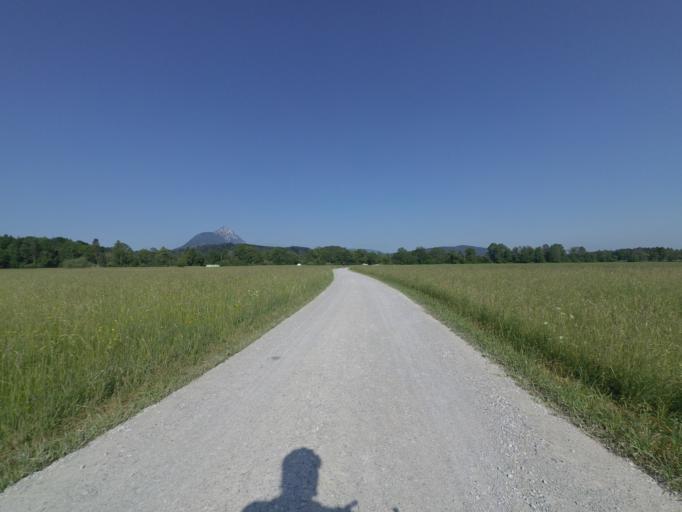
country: AT
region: Salzburg
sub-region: Politischer Bezirk Salzburg-Umgebung
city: Grodig
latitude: 47.7603
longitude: 12.9817
